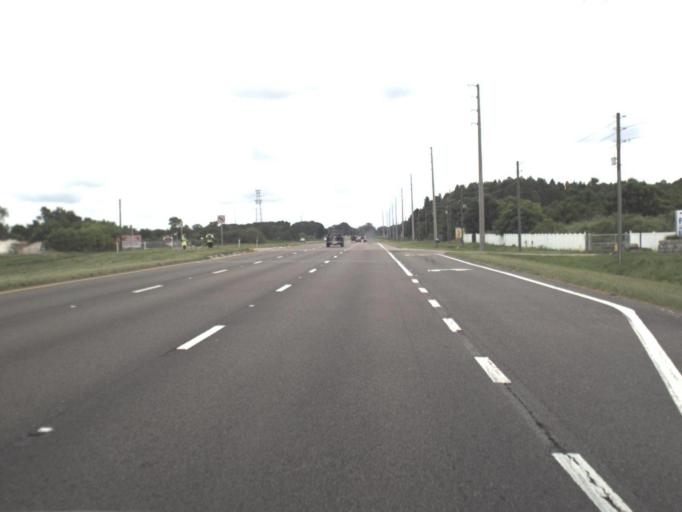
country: US
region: Florida
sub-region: Pasco County
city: Odessa
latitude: 28.1929
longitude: -82.5798
